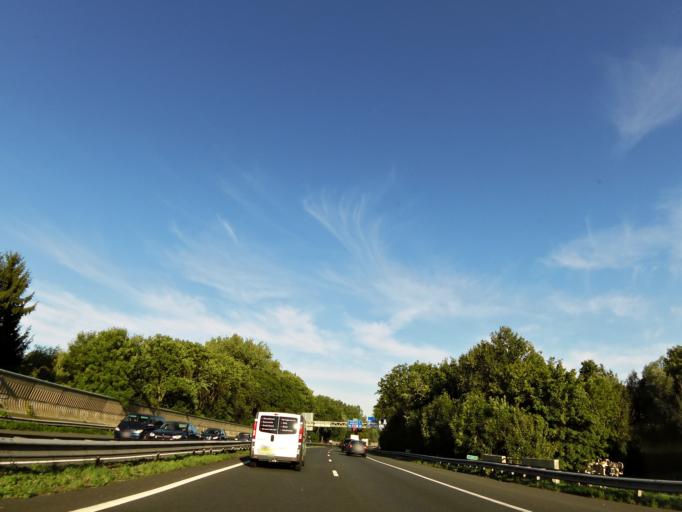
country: NL
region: Limburg
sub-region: Gemeente Nuth
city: Nuth
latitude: 50.9149
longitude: 5.9000
